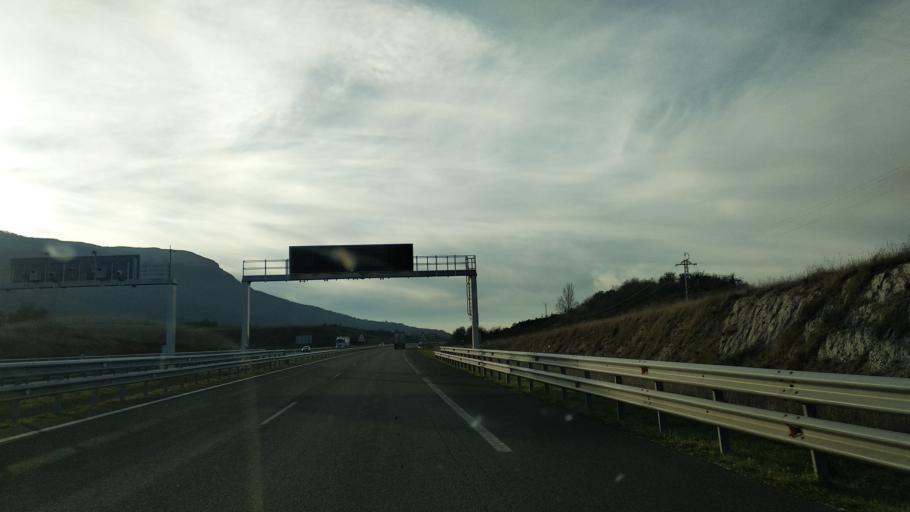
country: ES
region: Navarre
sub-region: Provincia de Navarra
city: Ziordia
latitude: 42.8653
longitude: -2.2519
